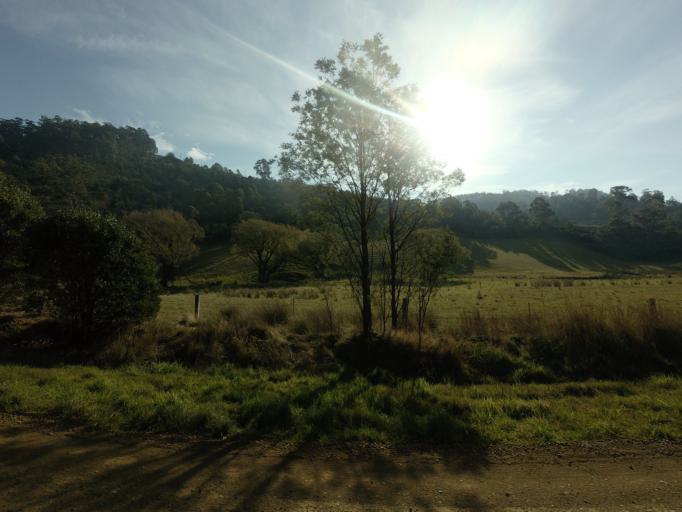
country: AU
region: Tasmania
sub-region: Sorell
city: Sorell
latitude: -42.5054
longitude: 147.4296
